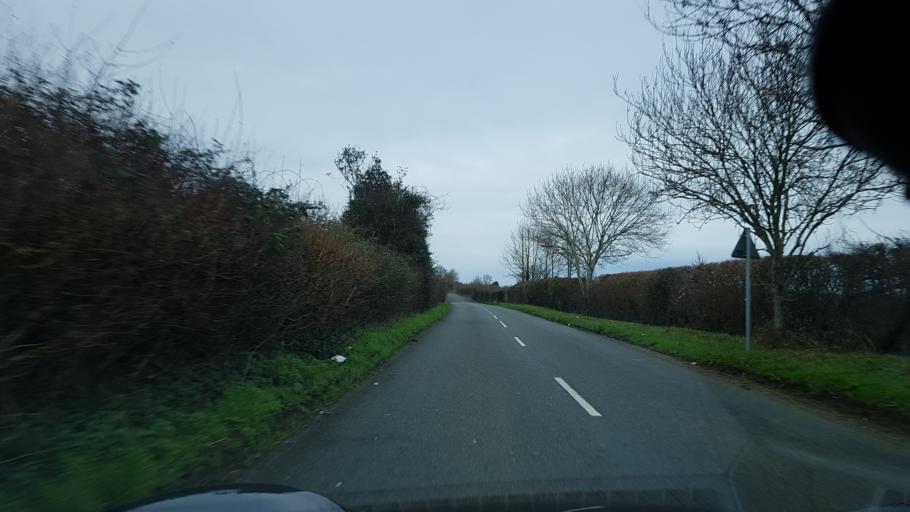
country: GB
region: England
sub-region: Somerset
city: Ilminster
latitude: 50.9501
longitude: -2.9522
